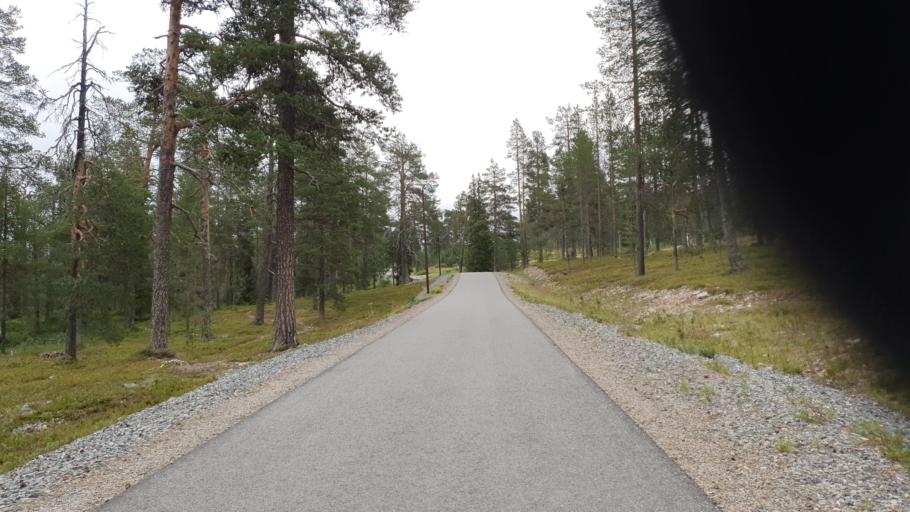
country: FI
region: Lapland
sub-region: Tunturi-Lappi
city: Kolari
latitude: 67.5946
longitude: 24.1901
